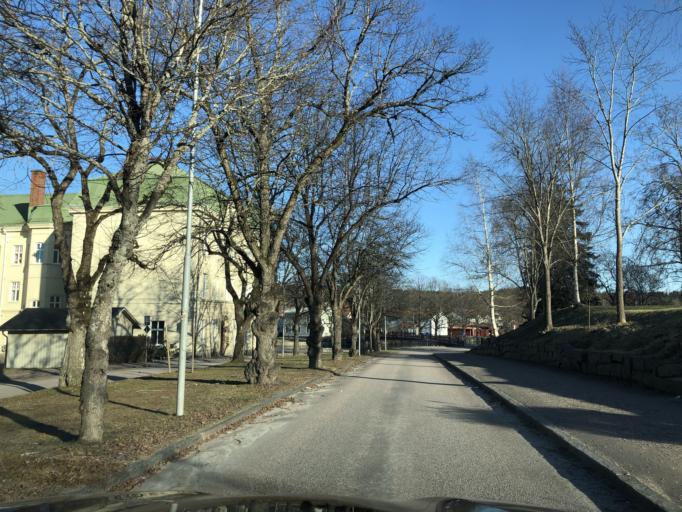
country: SE
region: Vaermland
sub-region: Filipstads Kommun
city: Filipstad
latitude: 59.7106
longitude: 14.1654
